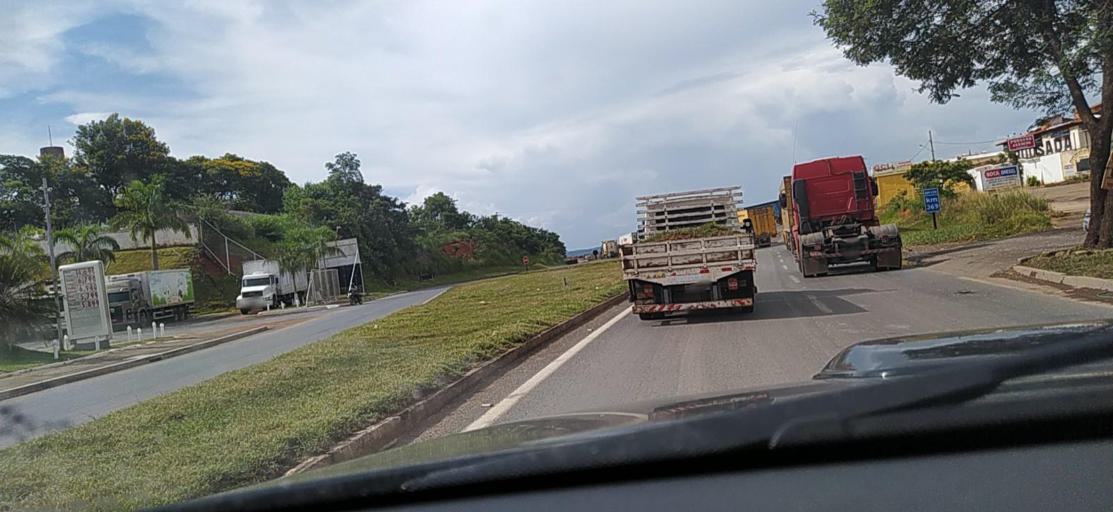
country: BR
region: Minas Gerais
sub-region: Montes Claros
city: Montes Claros
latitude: -16.7579
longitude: -43.8442
